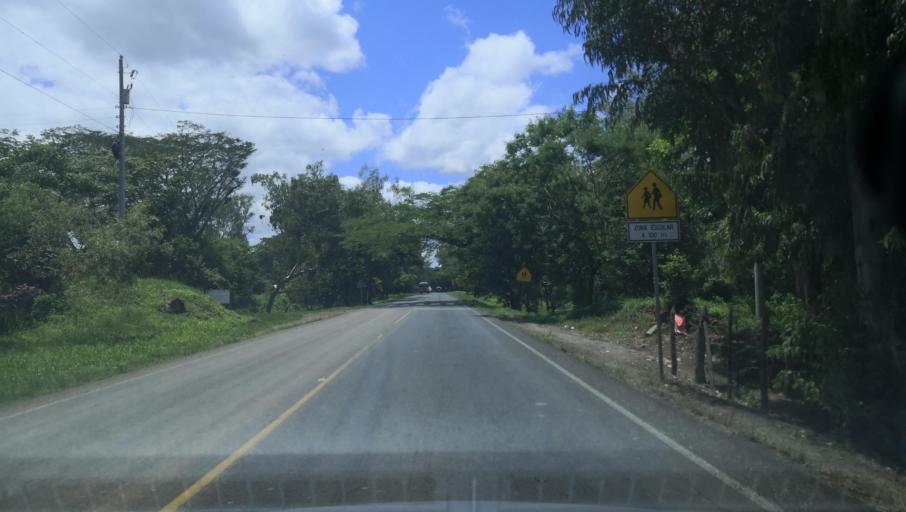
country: NI
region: Esteli
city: Condega
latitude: 13.2437
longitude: -86.3735
